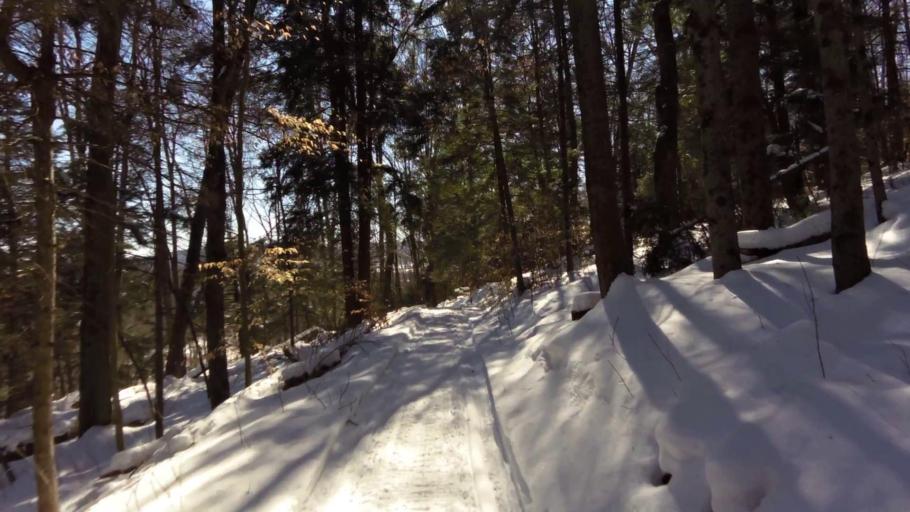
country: US
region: New York
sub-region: Allegany County
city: Cuba
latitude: 42.2817
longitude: -78.2322
